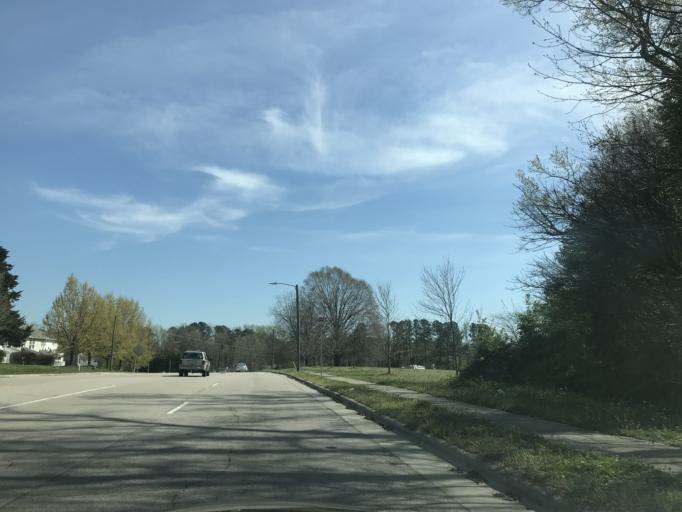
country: US
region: North Carolina
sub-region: Wake County
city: Raleigh
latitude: 35.8322
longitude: -78.5797
